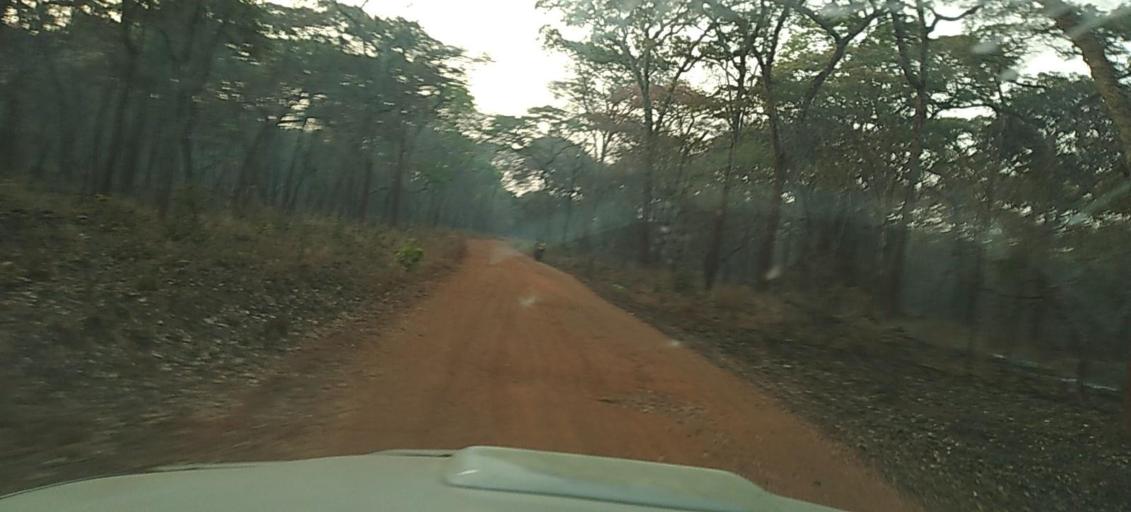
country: ZM
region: North-Western
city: Kasempa
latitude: -13.0922
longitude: 26.4002
